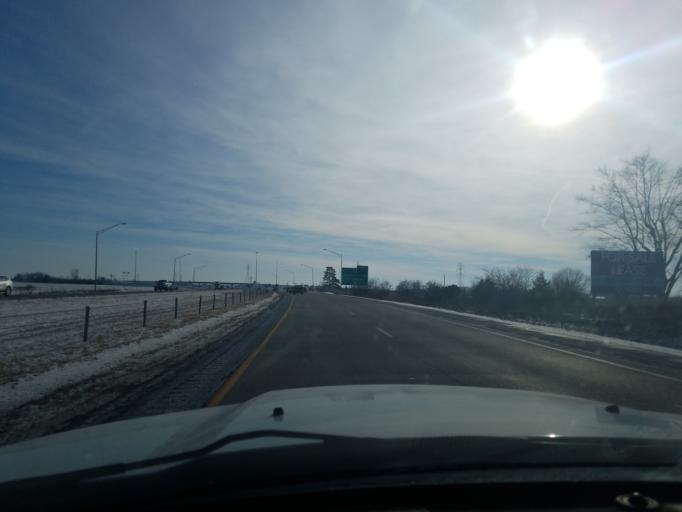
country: US
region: Indiana
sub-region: Grant County
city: Upland
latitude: 40.4292
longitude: -85.5493
